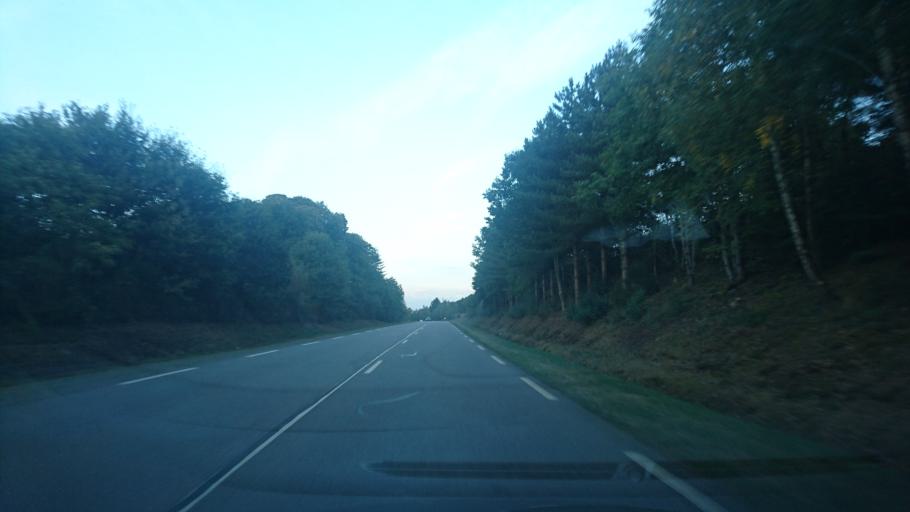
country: FR
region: Brittany
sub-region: Departement d'Ille-et-Vilaine
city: Lassy
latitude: 47.9629
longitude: -1.8778
